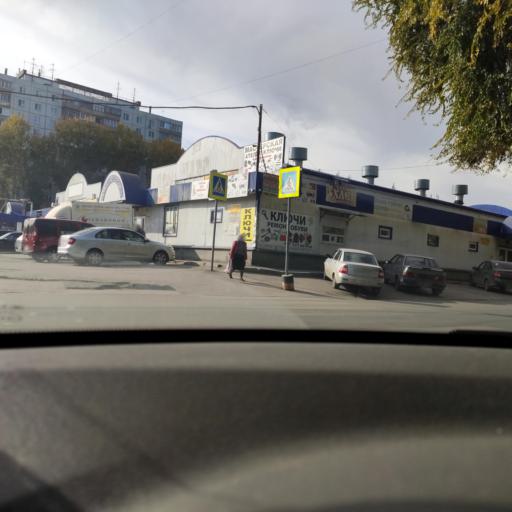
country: RU
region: Samara
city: Samara
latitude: 53.2445
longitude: 50.2534
